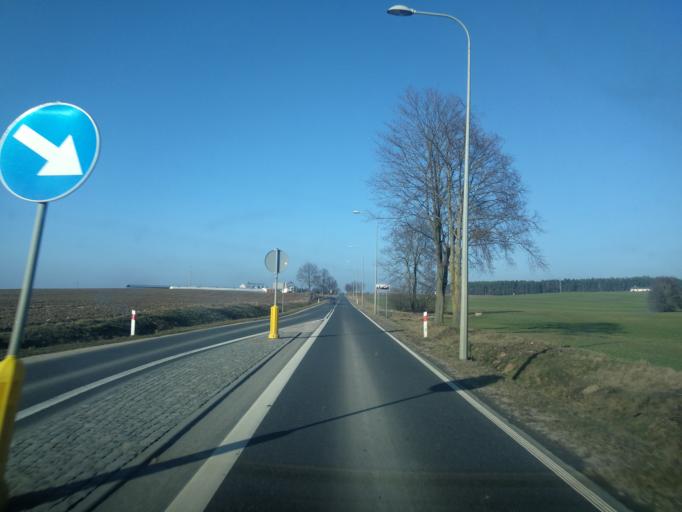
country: PL
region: Warmian-Masurian Voivodeship
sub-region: Powiat ilawski
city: Lubawa
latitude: 53.4300
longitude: 19.7739
